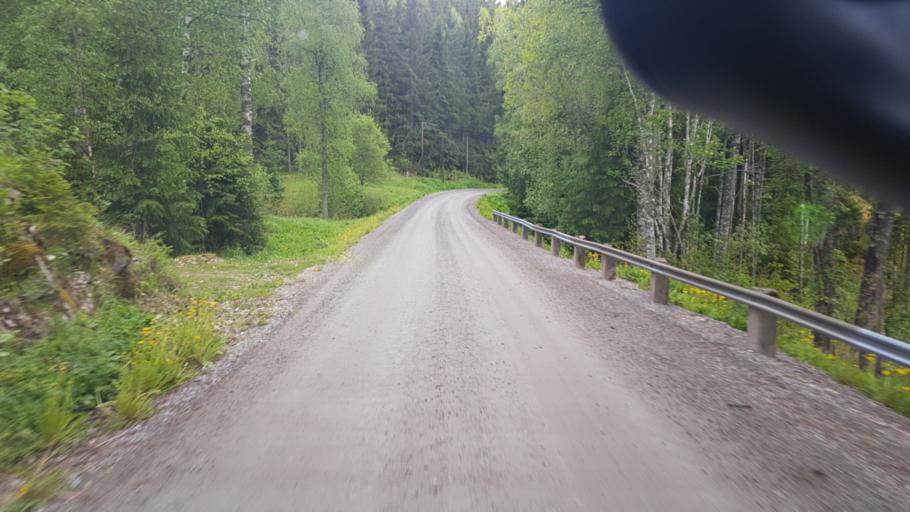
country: NO
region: Ostfold
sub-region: Romskog
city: Romskog
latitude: 59.7100
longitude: 11.9686
